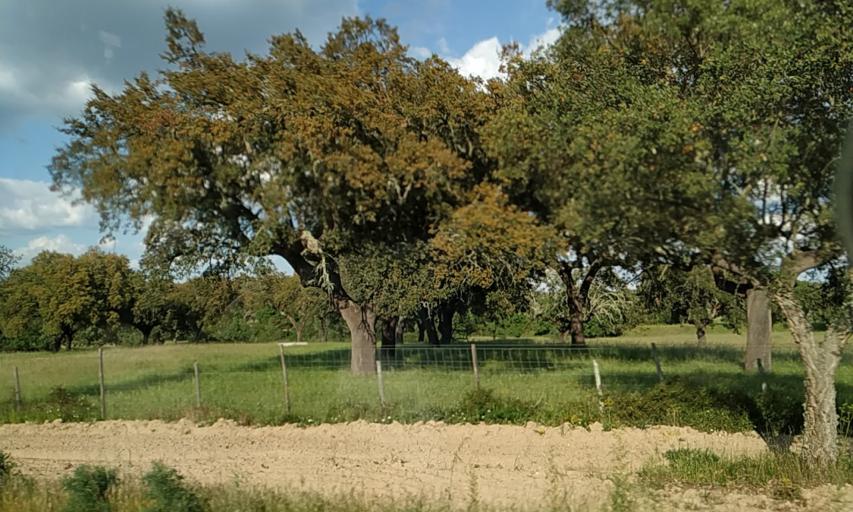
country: PT
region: Portalegre
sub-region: Portalegre
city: Urra
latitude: 39.2157
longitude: -7.4585
